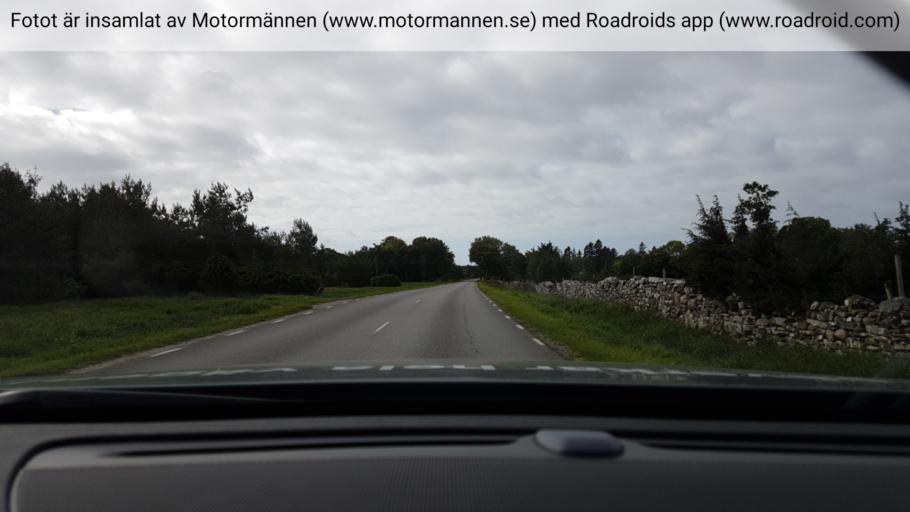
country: SE
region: Gotland
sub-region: Gotland
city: Hemse
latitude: 56.9643
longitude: 18.2258
